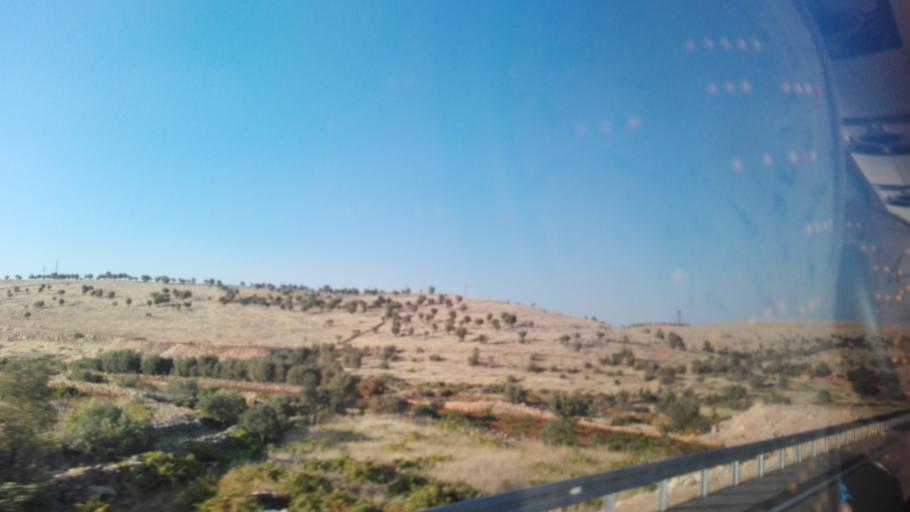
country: TR
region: Mardin
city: Ortaca
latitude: 37.5249
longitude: 41.5938
